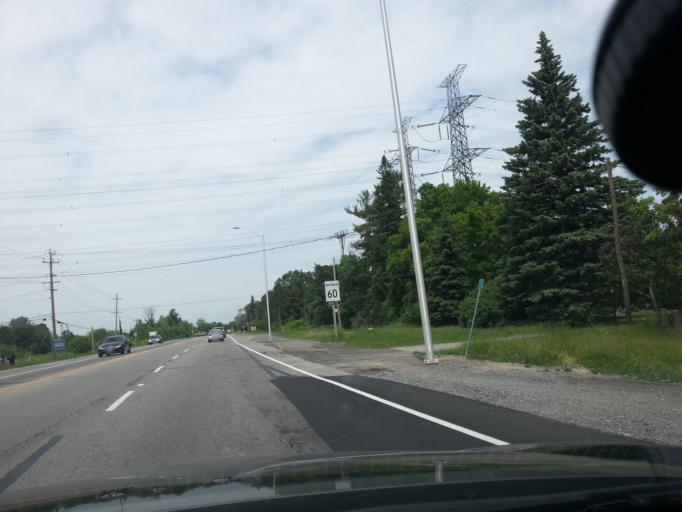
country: CA
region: Ontario
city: Ottawa
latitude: 45.3469
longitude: -75.7013
